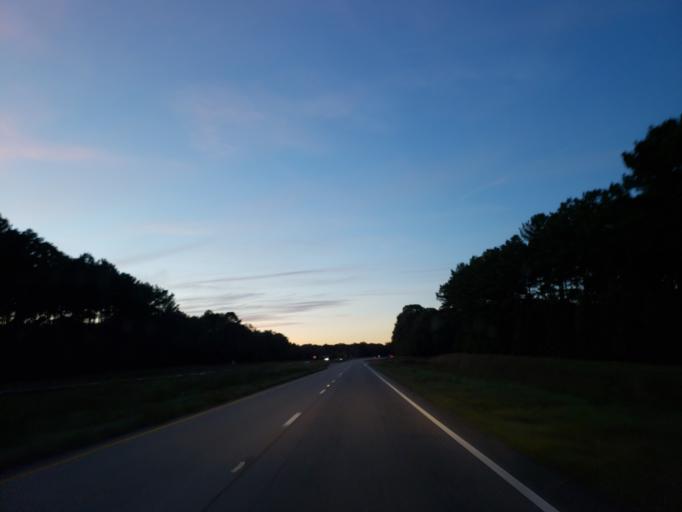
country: US
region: Mississippi
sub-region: Wayne County
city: Waynesboro
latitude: 31.8455
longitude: -88.7123
